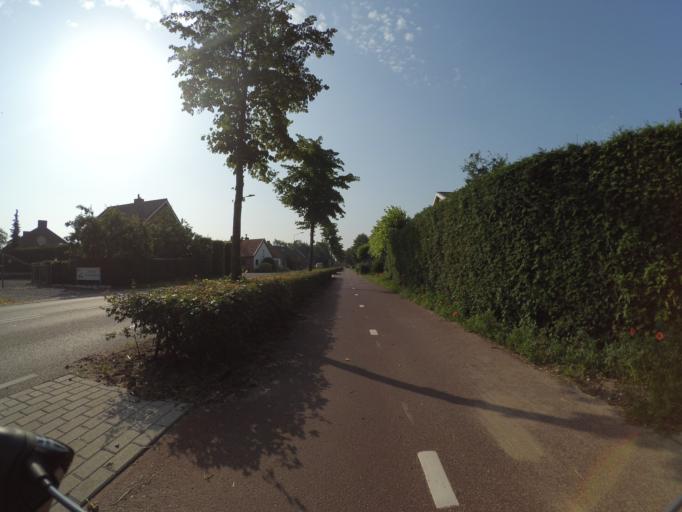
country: NL
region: North Brabant
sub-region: Gemeente Dongen
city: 's Gravenmoer
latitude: 51.6444
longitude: 4.9472
